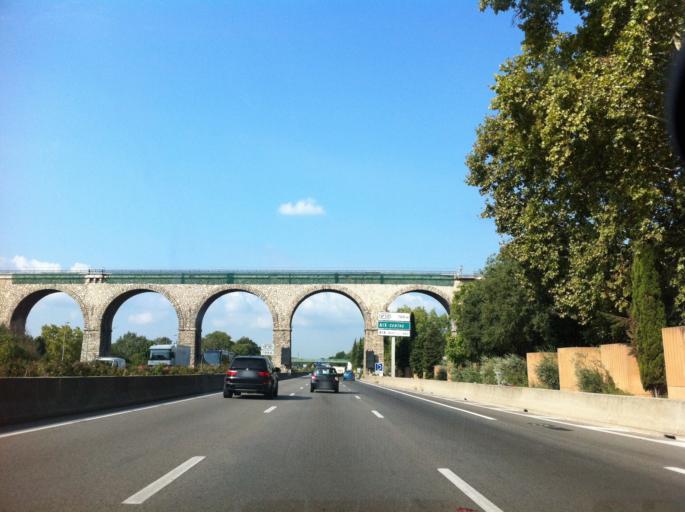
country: FR
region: Provence-Alpes-Cote d'Azur
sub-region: Departement des Bouches-du-Rhone
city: Aix-en-Provence
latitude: 43.5121
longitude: 5.4565
